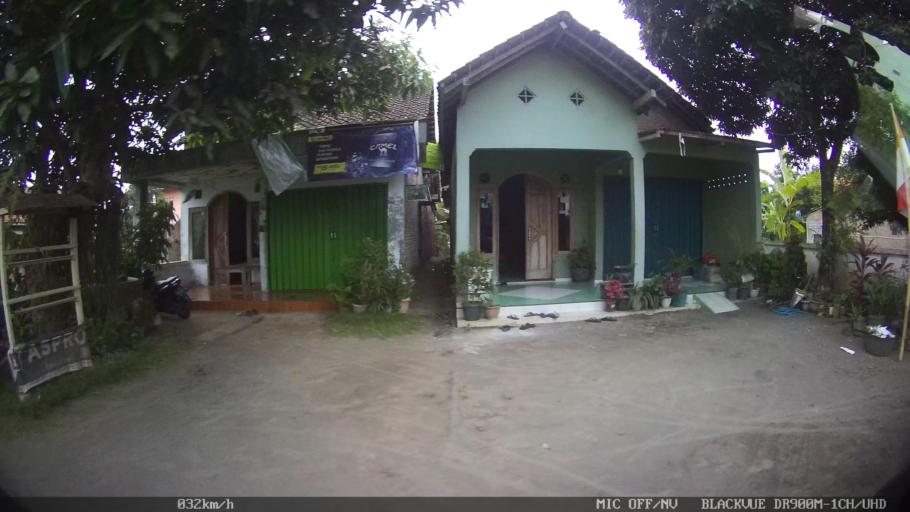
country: ID
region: Daerah Istimewa Yogyakarta
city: Sewon
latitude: -7.8535
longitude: 110.3966
